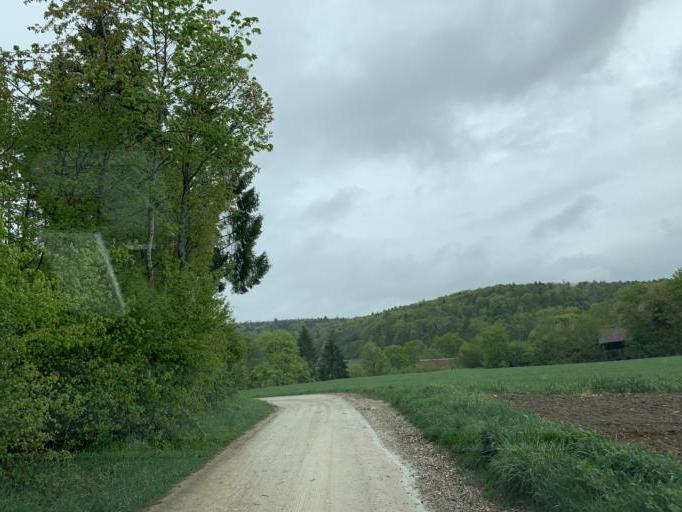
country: CH
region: Schaffhausen
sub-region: Bezirk Schaffhausen
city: Beringen
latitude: 47.7057
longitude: 8.5923
